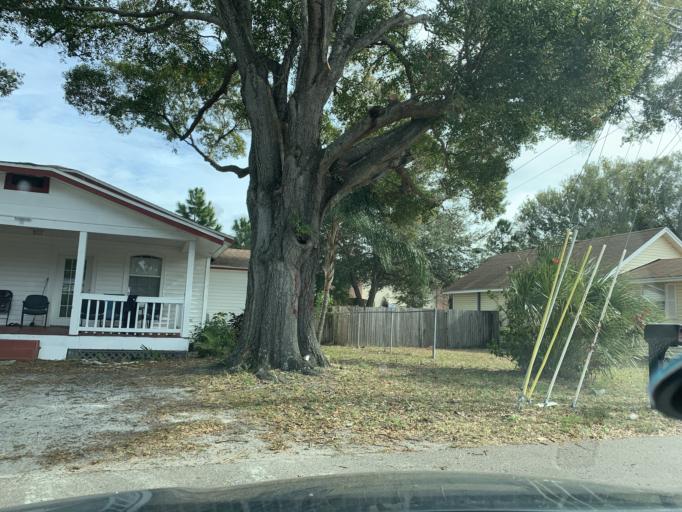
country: US
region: Florida
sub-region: Pinellas County
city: Largo
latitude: 27.8927
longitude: -82.7883
